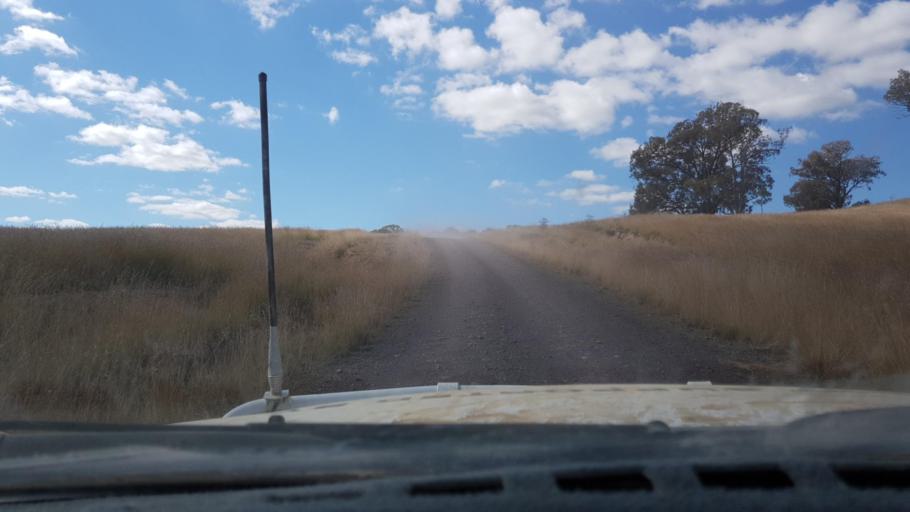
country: AU
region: New South Wales
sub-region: Tamworth Municipality
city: Manilla
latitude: -30.4270
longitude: 150.8120
